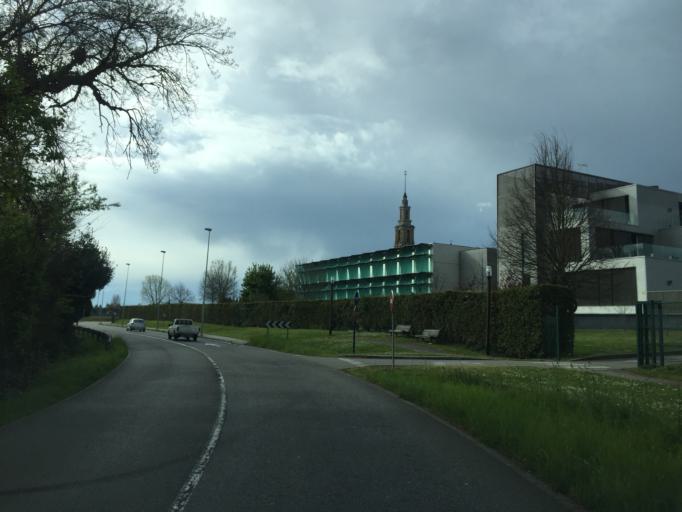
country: ES
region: Asturias
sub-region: Province of Asturias
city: Gijon
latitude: 43.5216
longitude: -5.6119
